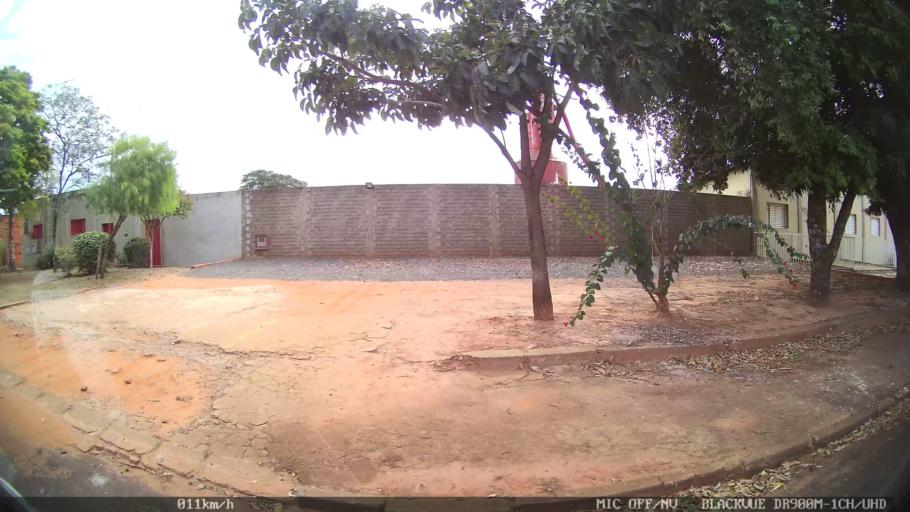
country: BR
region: Sao Paulo
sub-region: Bady Bassitt
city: Bady Bassitt
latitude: -20.8102
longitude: -49.5028
